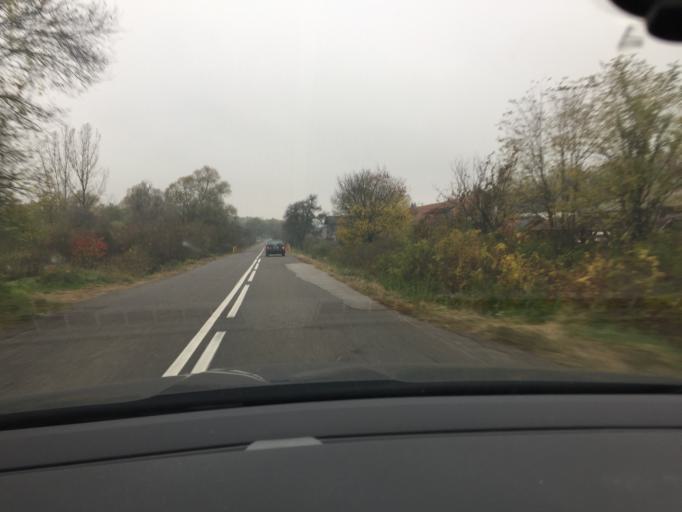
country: SK
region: Banskobystricky
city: Dudince
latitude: 48.1507
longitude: 18.9078
